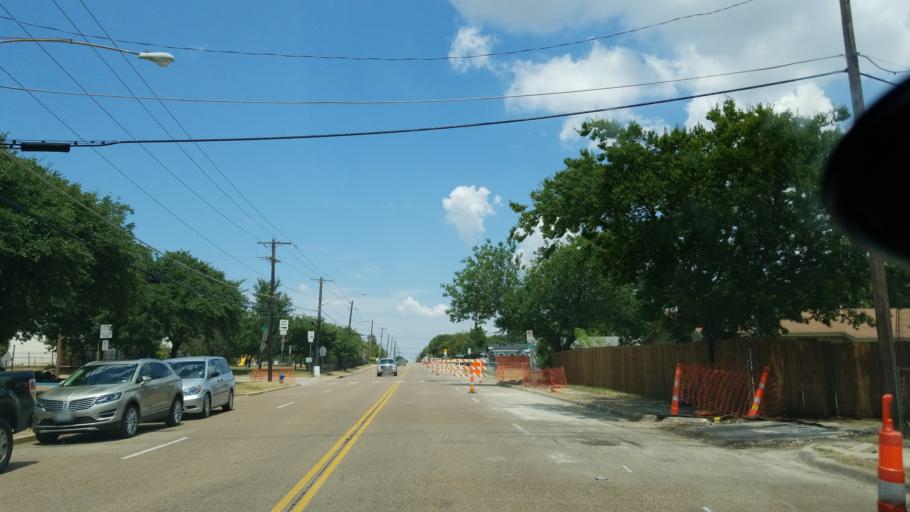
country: US
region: Texas
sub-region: Dallas County
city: Cockrell Hill
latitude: 32.7160
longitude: -96.9001
